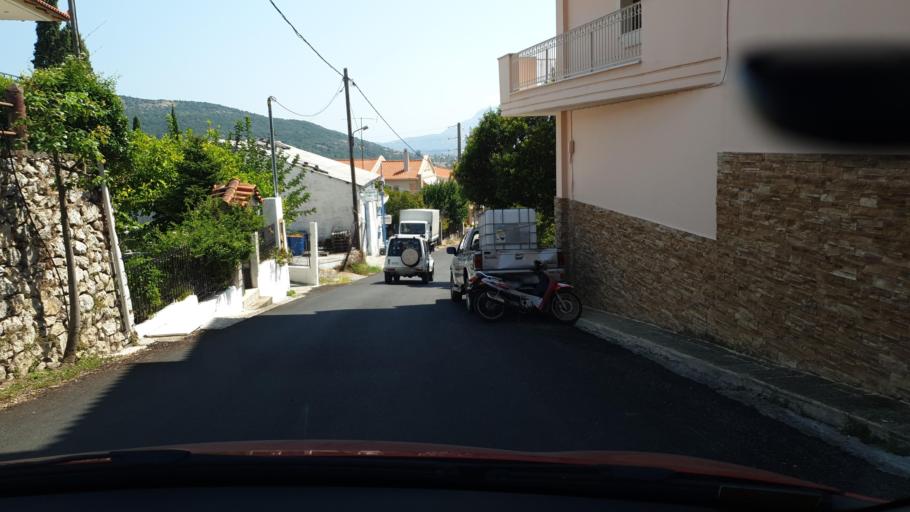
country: GR
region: Central Greece
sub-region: Nomos Evvoias
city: Oxilithos
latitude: 38.5773
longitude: 24.0603
